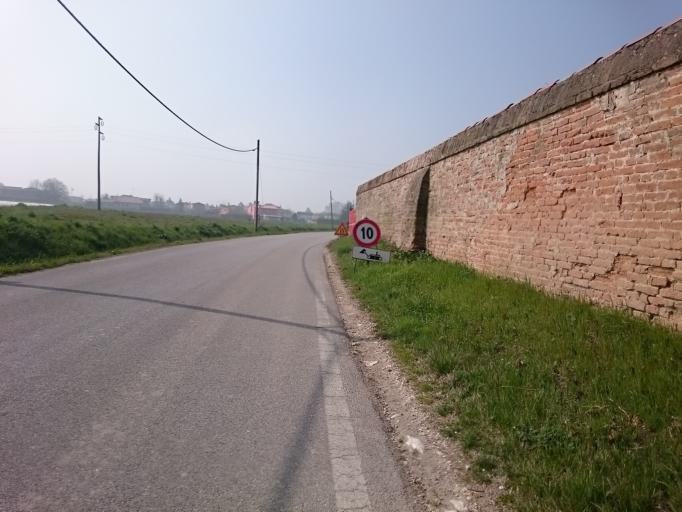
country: IT
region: Veneto
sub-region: Provincia di Padova
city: Pernumia
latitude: 45.2607
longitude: 11.7963
